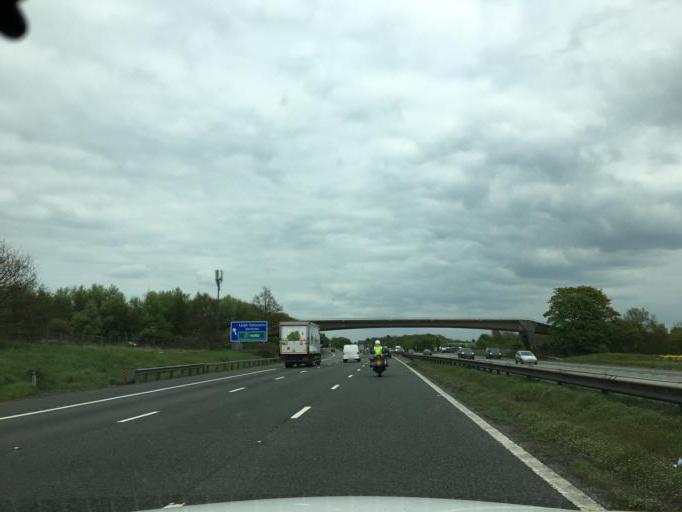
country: GB
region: England
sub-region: Wiltshire
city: Norton
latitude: 51.5098
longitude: -2.1687
